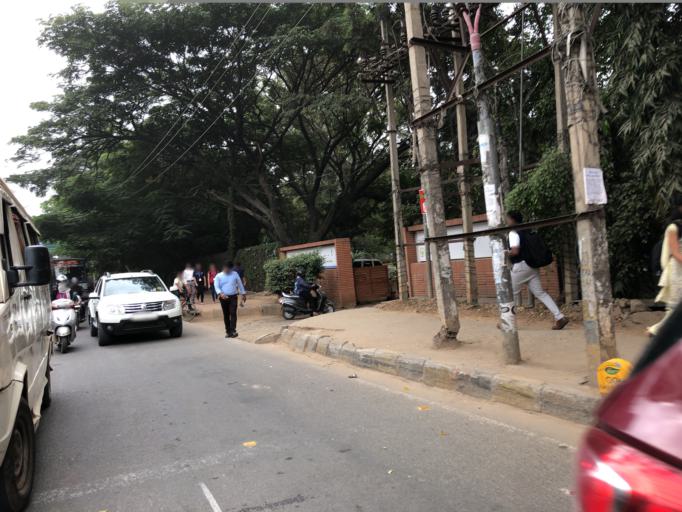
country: IN
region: Karnataka
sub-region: Bangalore Rural
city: Hoskote
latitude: 12.9881
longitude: 77.7317
